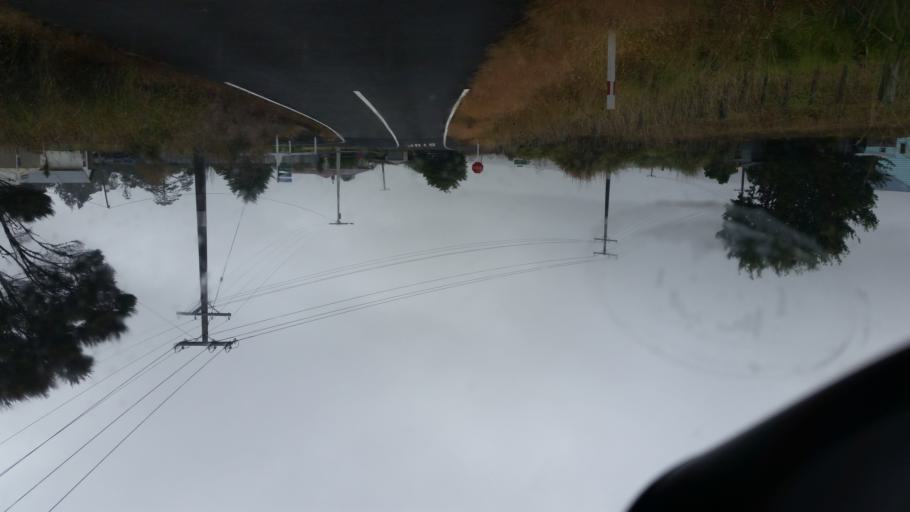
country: NZ
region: Northland
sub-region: Kaipara District
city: Dargaville
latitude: -35.8343
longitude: 173.7525
